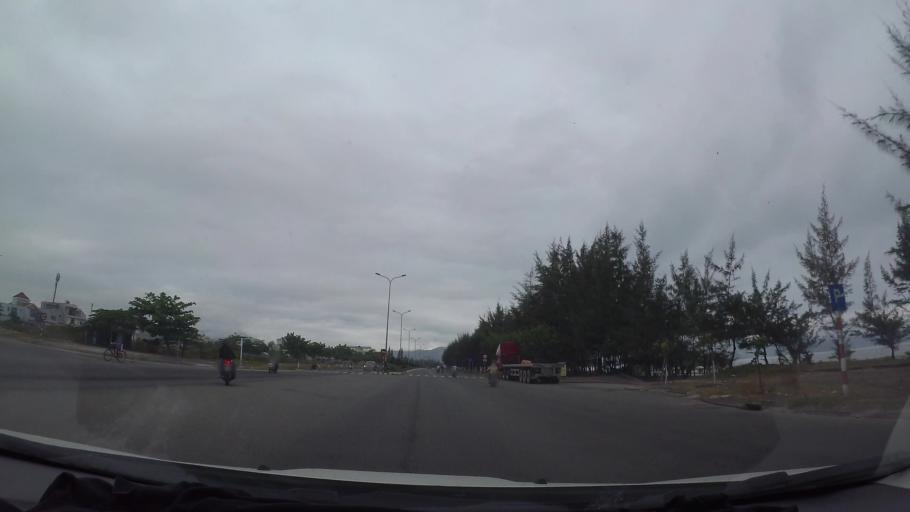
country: VN
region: Da Nang
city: Lien Chieu
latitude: 16.0906
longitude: 108.1517
